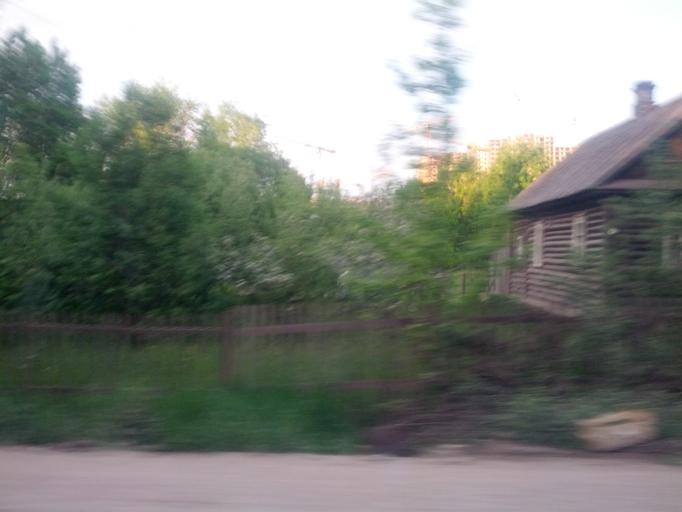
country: RU
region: Leningrad
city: Rybatskoye
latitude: 59.9077
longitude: 30.5064
